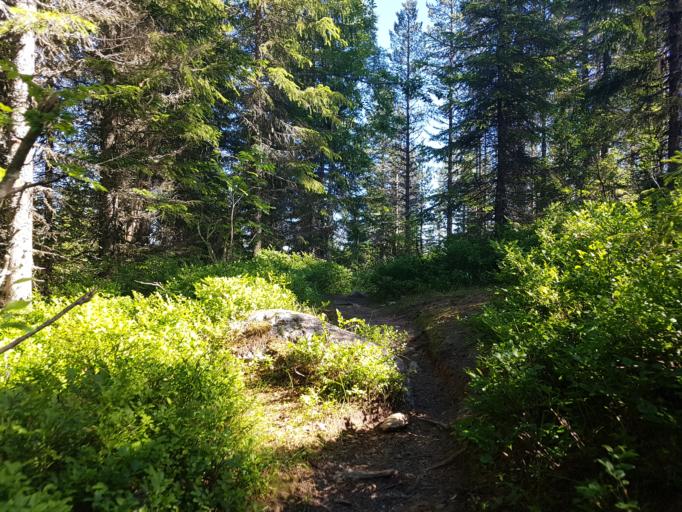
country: NO
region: Sor-Trondelag
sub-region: Trondheim
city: Trondheim
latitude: 63.4369
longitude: 10.2724
